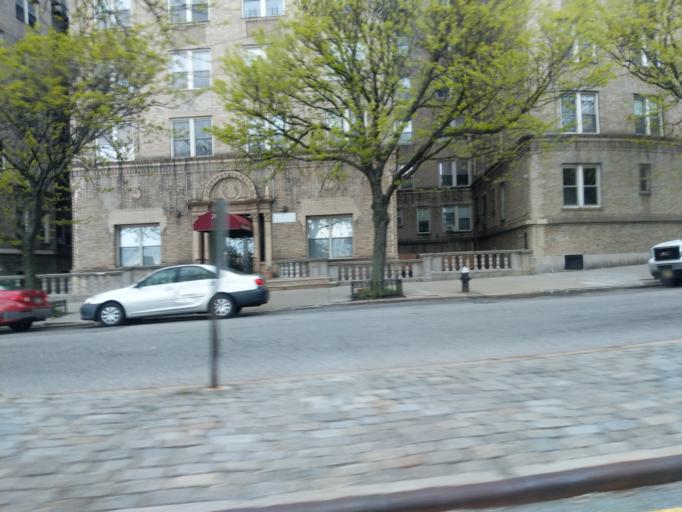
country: US
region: New Jersey
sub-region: Bergen County
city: Fort Lee
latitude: 40.8343
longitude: -73.9487
